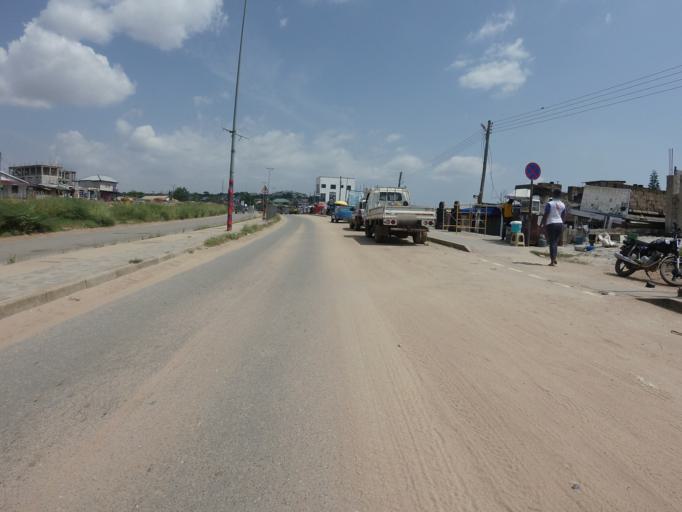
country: GH
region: Greater Accra
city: Gbawe
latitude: 5.6270
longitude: -0.3109
